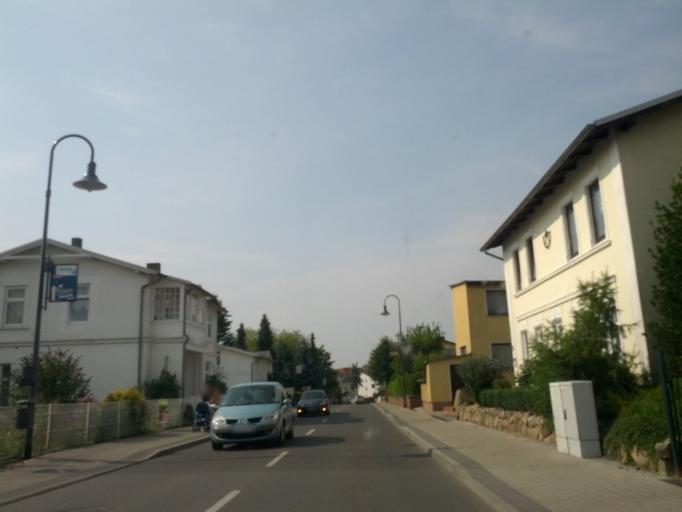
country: DE
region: Mecklenburg-Vorpommern
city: Ostseebad Binz
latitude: 54.3933
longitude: 13.6097
